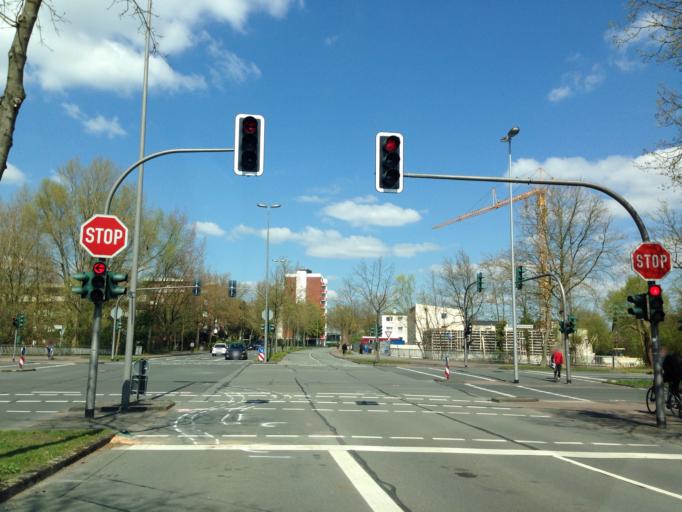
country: DE
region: North Rhine-Westphalia
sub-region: Regierungsbezirk Munster
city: Muenster
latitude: 51.9696
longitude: 7.5965
